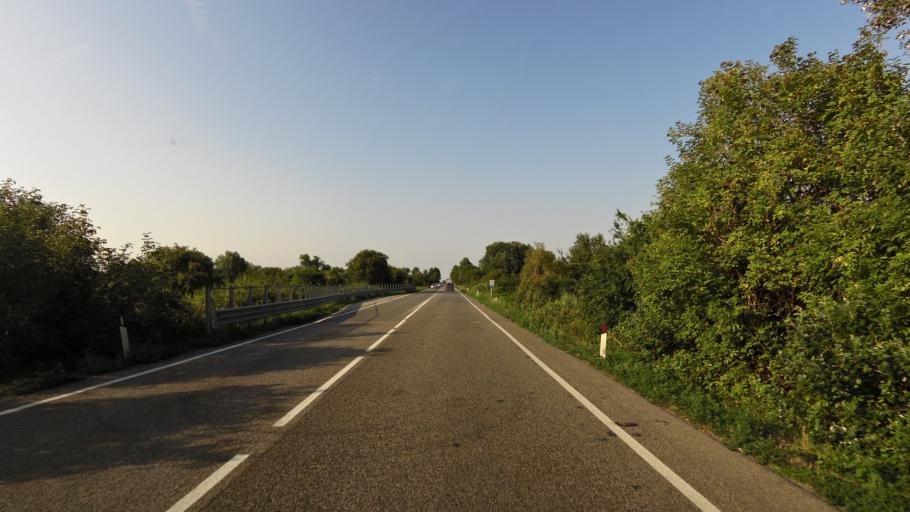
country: IT
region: Emilia-Romagna
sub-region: Provincia di Ravenna
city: Marina Romea
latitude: 44.5426
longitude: 12.2362
